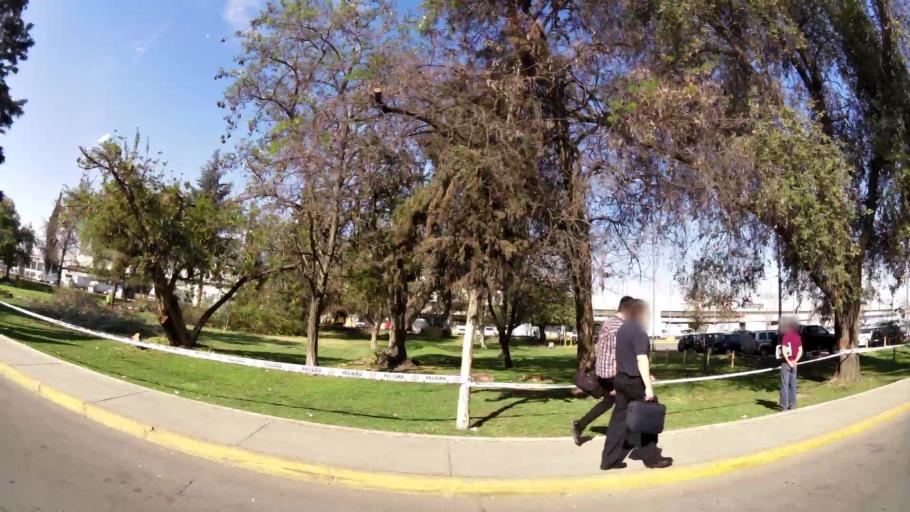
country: CL
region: Santiago Metropolitan
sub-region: Provincia de Santiago
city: Lo Prado
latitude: -33.4035
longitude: -70.7919
